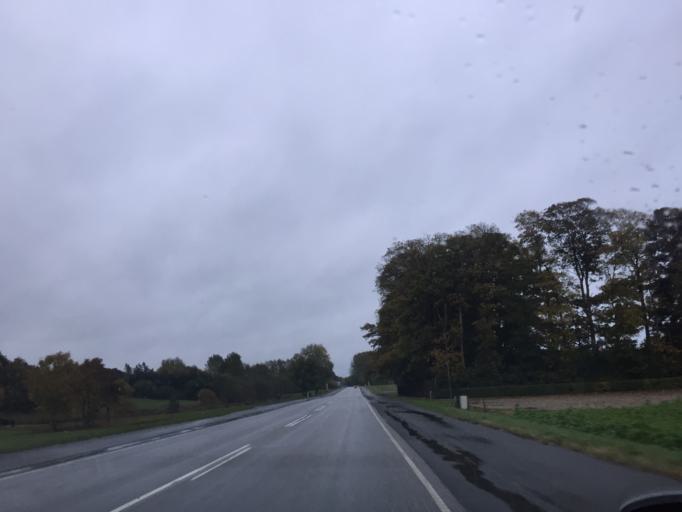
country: DK
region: Zealand
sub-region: Ringsted Kommune
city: Ringsted
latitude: 55.4703
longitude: 11.7467
